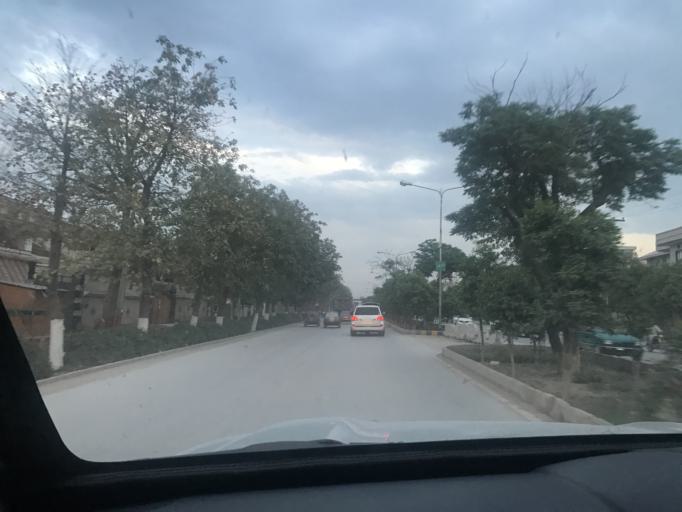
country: PK
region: Khyber Pakhtunkhwa
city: Peshawar
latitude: 33.9774
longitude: 71.4480
